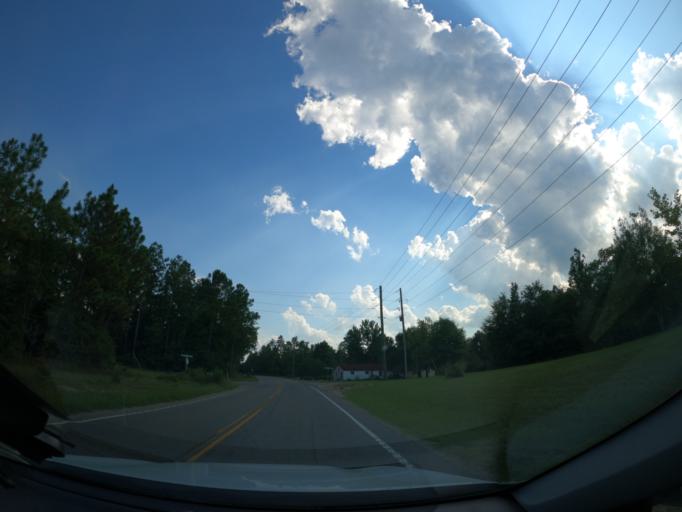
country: US
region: South Carolina
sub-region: Barnwell County
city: Williston
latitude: 33.5163
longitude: -81.5045
